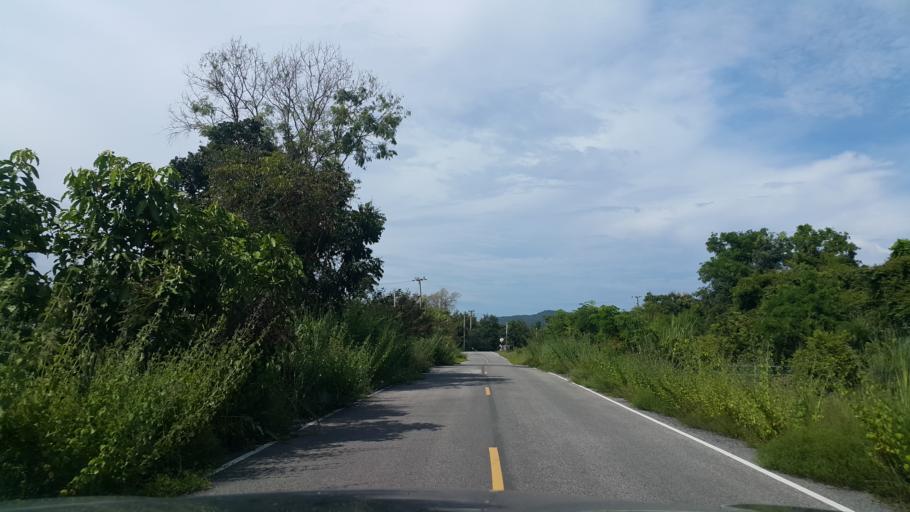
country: TH
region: Chiang Mai
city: Mae On
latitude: 18.8235
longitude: 99.1854
